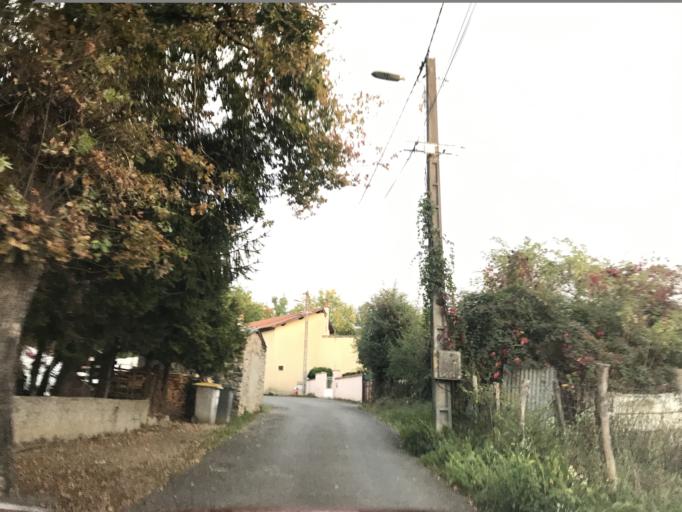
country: FR
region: Auvergne
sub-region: Departement du Puy-de-Dome
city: Thiers
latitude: 45.8438
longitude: 3.5408
